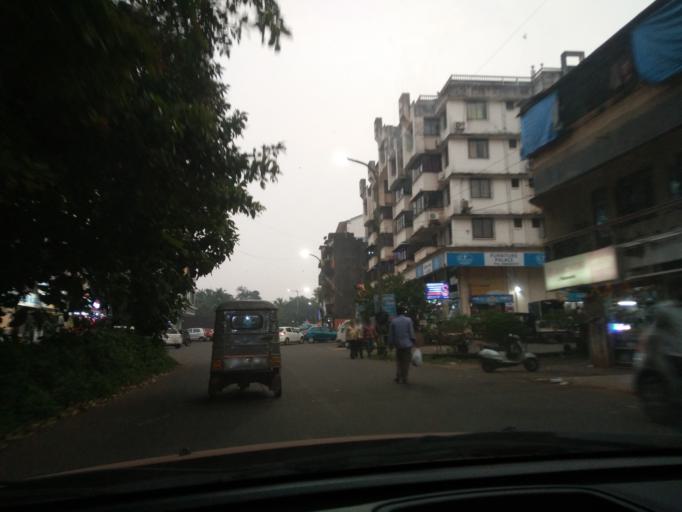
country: IN
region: Goa
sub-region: South Goa
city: Davorlim
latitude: 15.2833
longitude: 73.9782
